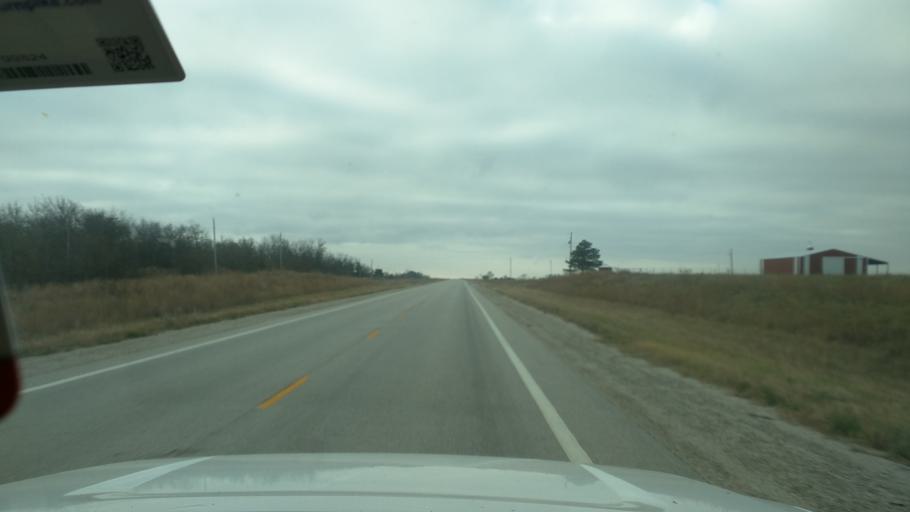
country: US
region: Kansas
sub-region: Elk County
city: Howard
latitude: 37.5803
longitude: -96.2533
